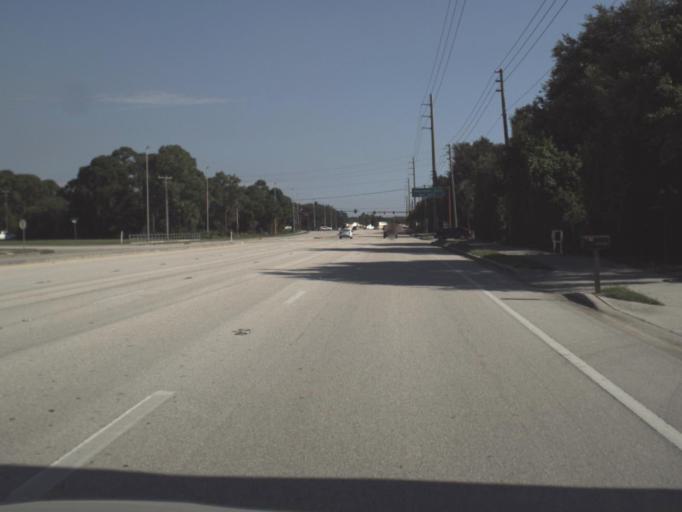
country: US
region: Florida
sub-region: Sarasota County
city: South Venice
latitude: 27.0438
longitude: -82.4023
